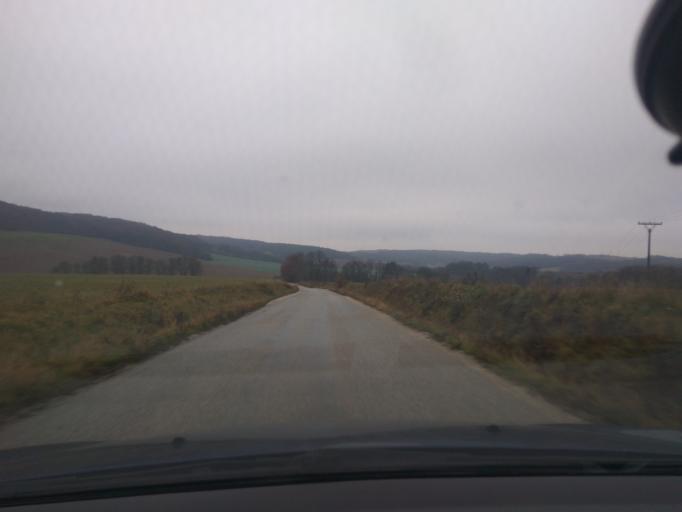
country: SK
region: Trnavsky
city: Vrbove
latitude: 48.6851
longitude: 17.6733
